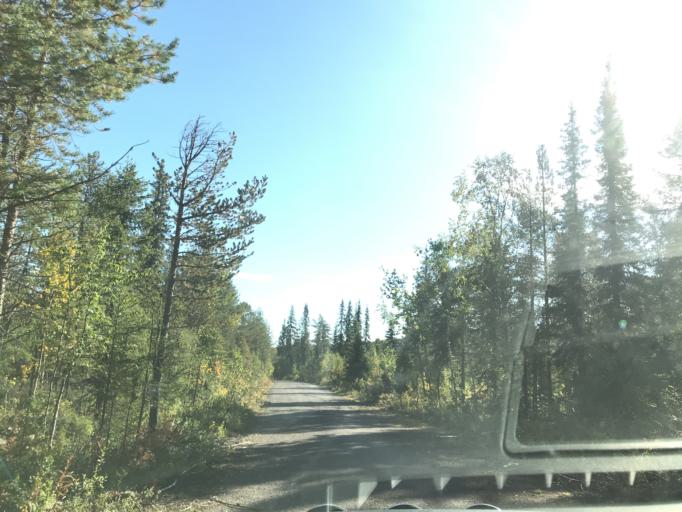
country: SE
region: Norrbotten
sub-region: Gallivare Kommun
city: Malmberget
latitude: 67.6466
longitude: 21.1028
